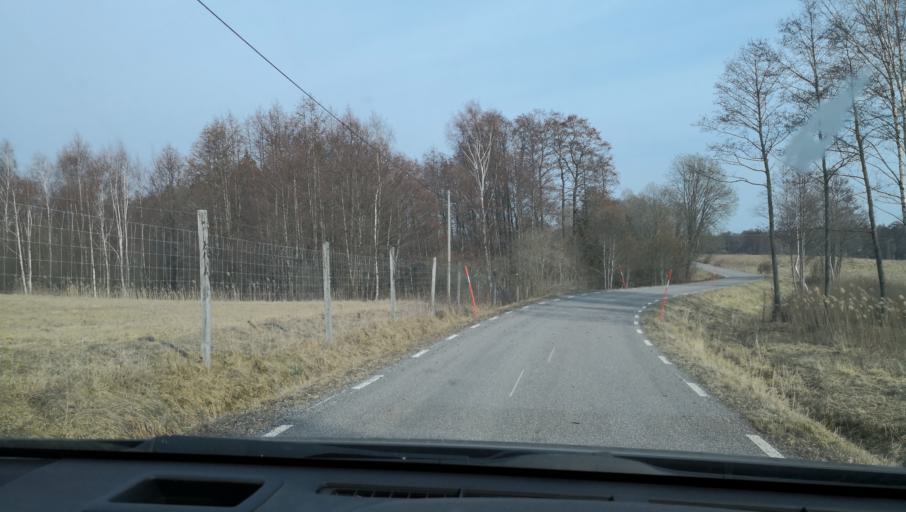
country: SE
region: OErebro
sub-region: Lindesbergs Kommun
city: Frovi
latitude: 59.3952
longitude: 15.4014
